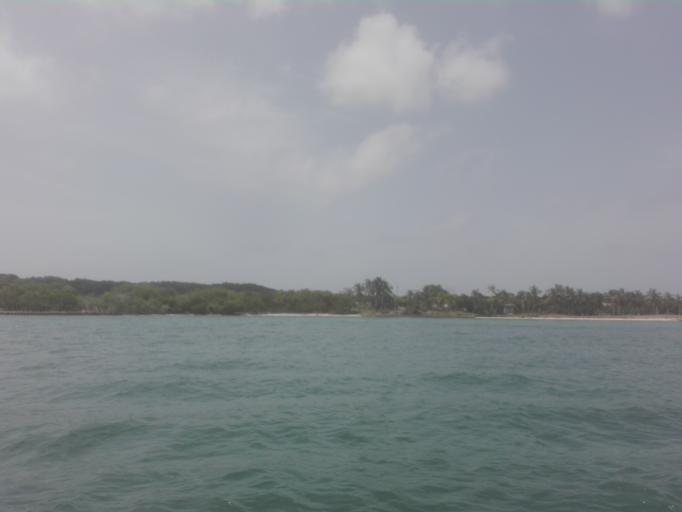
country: CO
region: Bolivar
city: Turbana
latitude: 10.1581
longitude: -75.6862
